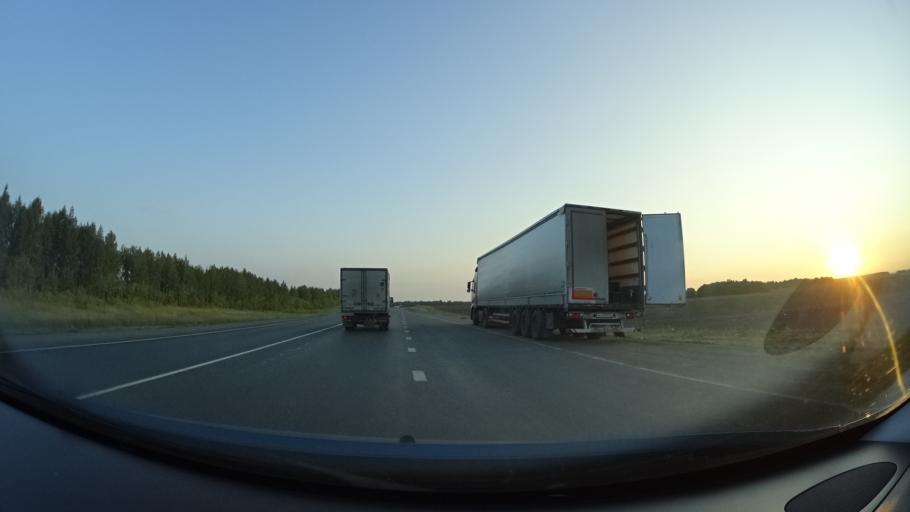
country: RU
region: Samara
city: Sernovodsk
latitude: 53.9308
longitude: 51.3294
